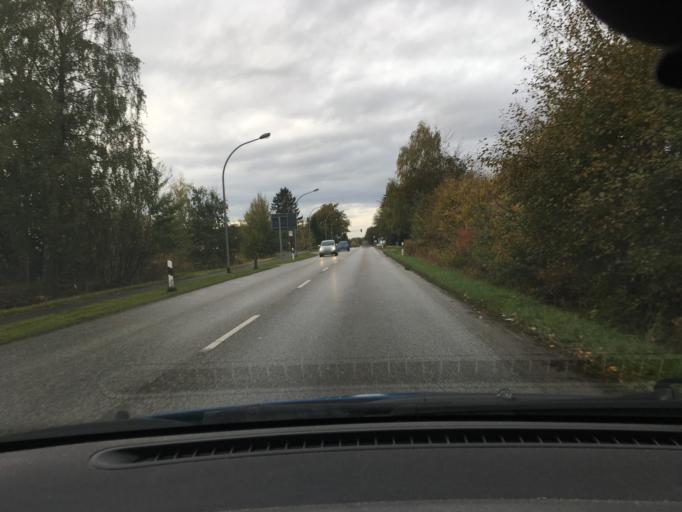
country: DE
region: Schleswig-Holstein
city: Bornsen
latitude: 53.4875
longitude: 10.2870
